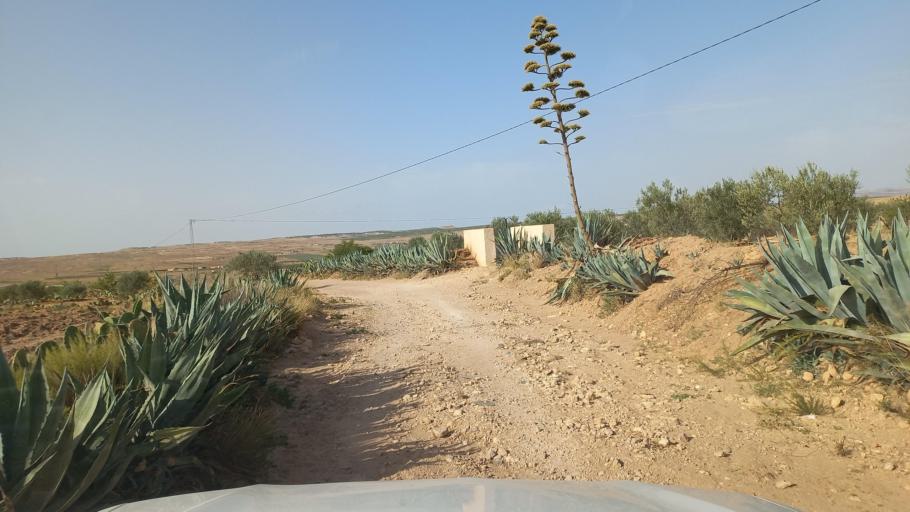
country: TN
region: Al Qasrayn
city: Kasserine
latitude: 35.3374
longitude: 8.8451
